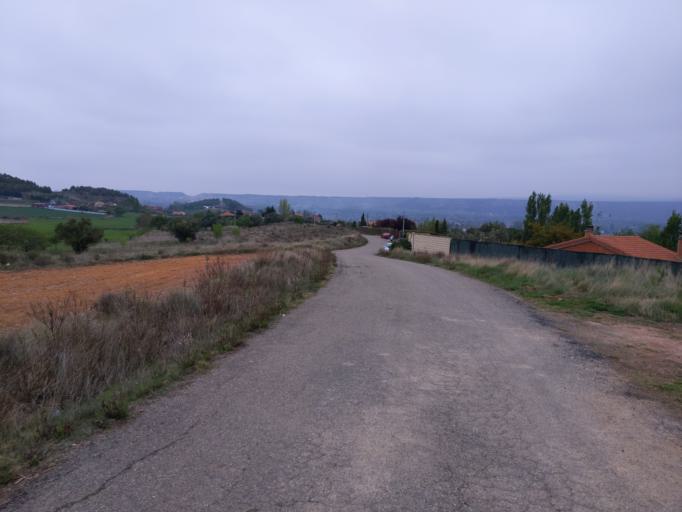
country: ES
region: La Rioja
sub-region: Provincia de La Rioja
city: Lardero
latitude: 42.4077
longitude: -2.4865
